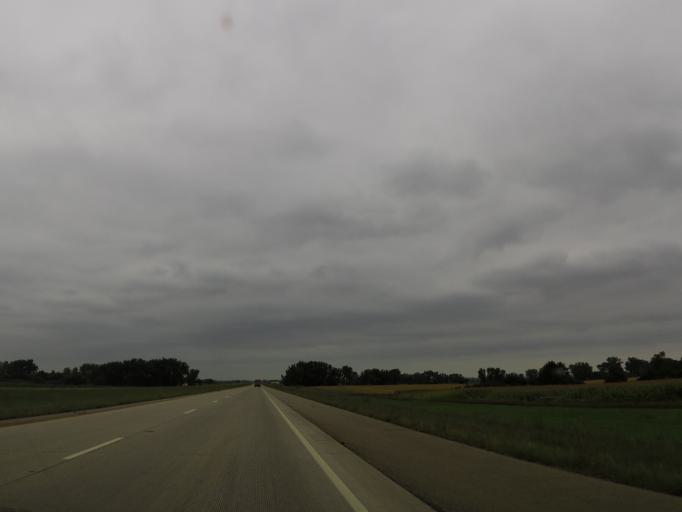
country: US
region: South Dakota
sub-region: Roberts County
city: Sisseton
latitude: 45.4954
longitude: -96.9891
